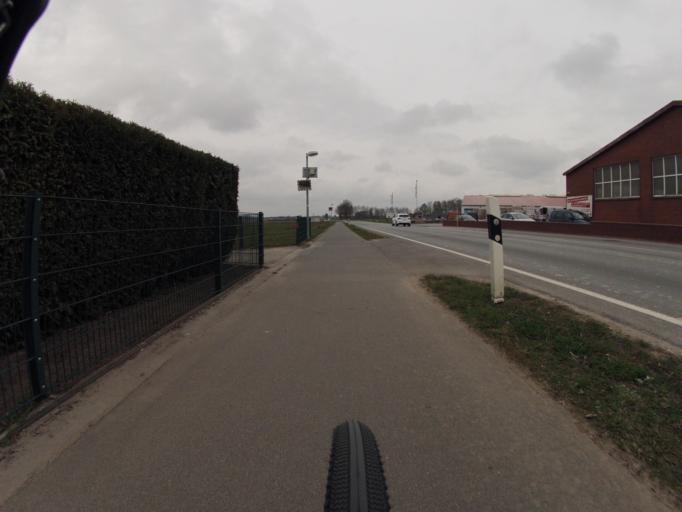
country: DE
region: North Rhine-Westphalia
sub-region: Regierungsbezirk Munster
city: Recke
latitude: 52.3394
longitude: 7.7390
